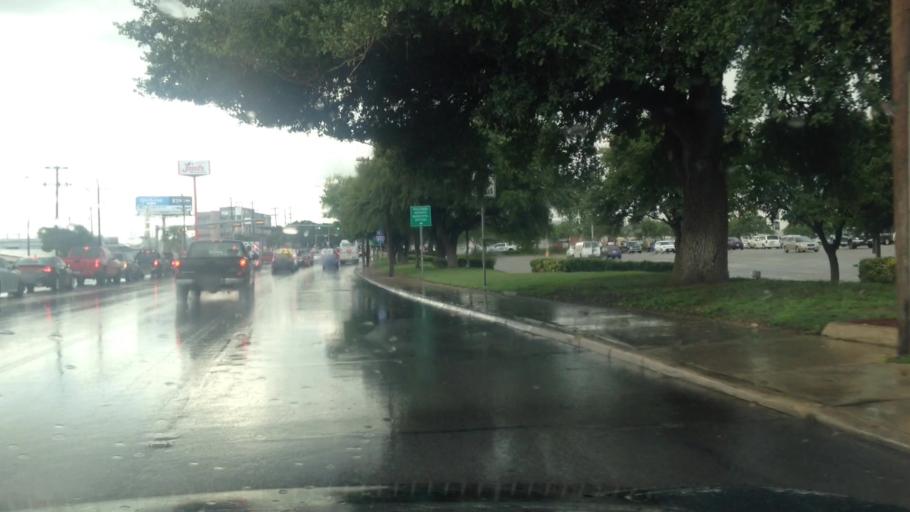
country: US
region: Texas
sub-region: Bexar County
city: Balcones Heights
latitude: 29.4913
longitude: -98.5525
